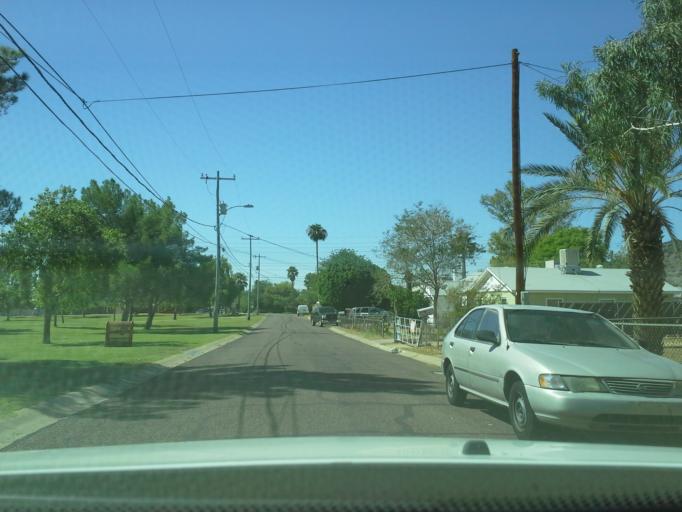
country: US
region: Arizona
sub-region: Maricopa County
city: Paradise Valley
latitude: 33.5723
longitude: -112.0551
